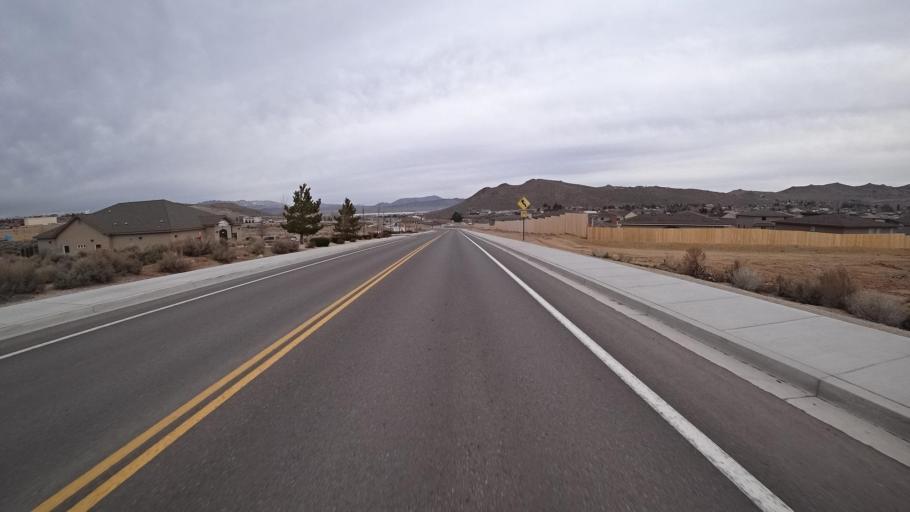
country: US
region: Nevada
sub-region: Washoe County
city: Golden Valley
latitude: 39.6111
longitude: -119.8449
